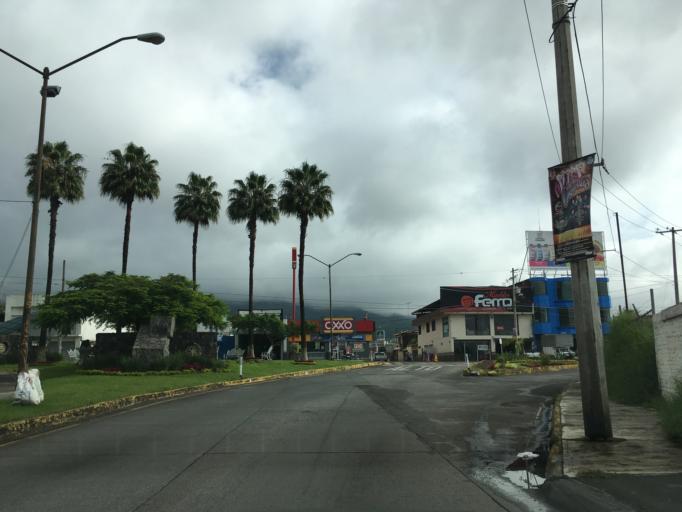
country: MX
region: Michoacan
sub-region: Uruapan
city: Uruapan
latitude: 19.4170
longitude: -102.0461
